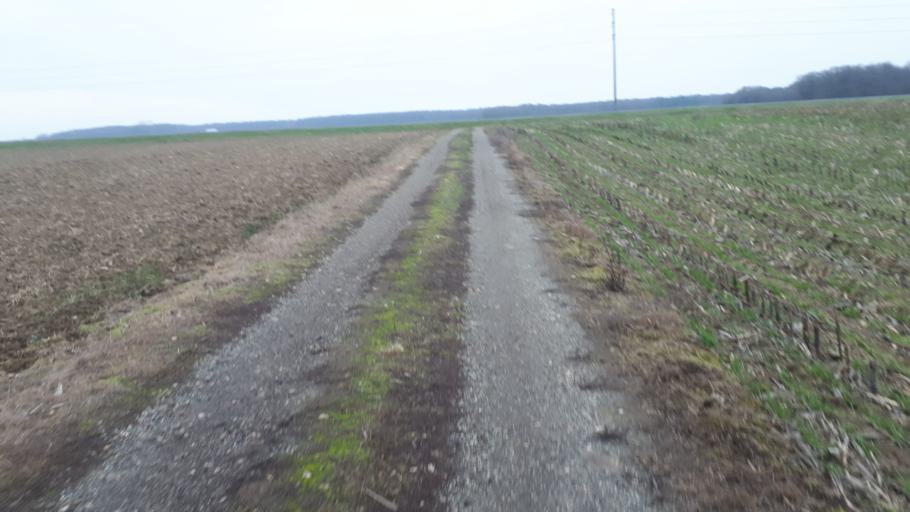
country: FR
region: Centre
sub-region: Departement du Loir-et-Cher
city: Villiers-sur-Loir
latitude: 47.8214
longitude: 1.0105
